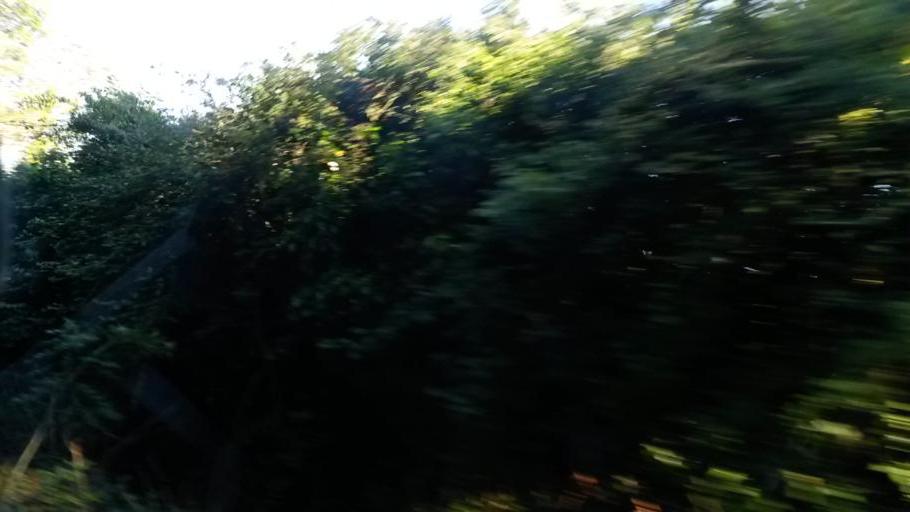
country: IE
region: Leinster
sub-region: Dublin City
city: Finglas
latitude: 53.4573
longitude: -6.3188
